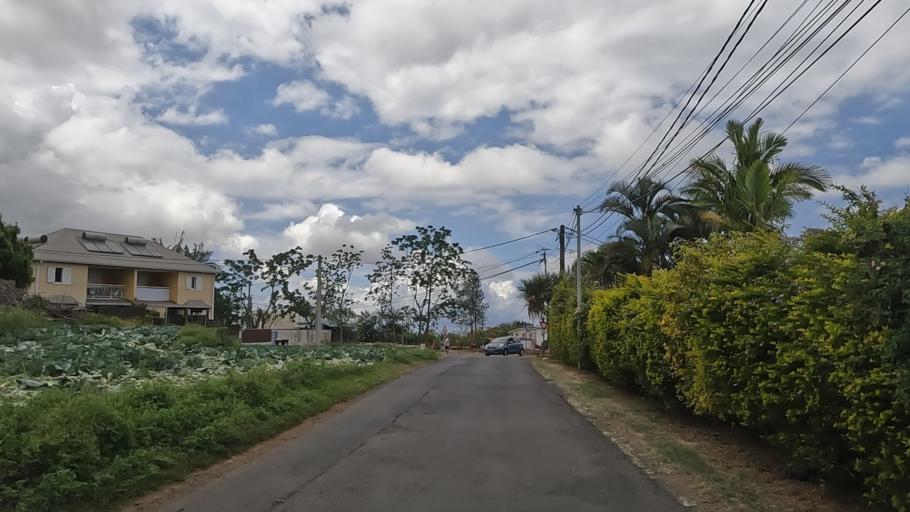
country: RE
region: Reunion
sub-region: Reunion
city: Le Tampon
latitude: -21.2624
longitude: 55.5175
